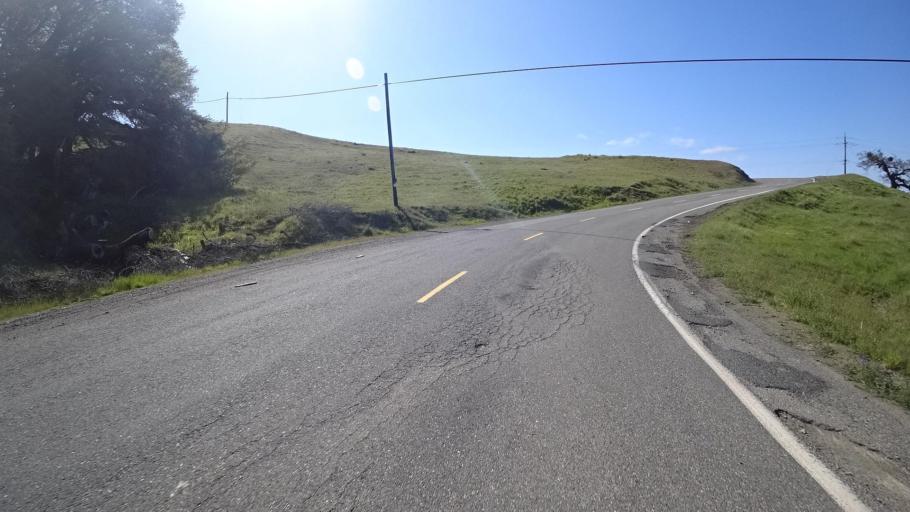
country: US
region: California
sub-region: Humboldt County
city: Redway
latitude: 40.1040
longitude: -123.6920
